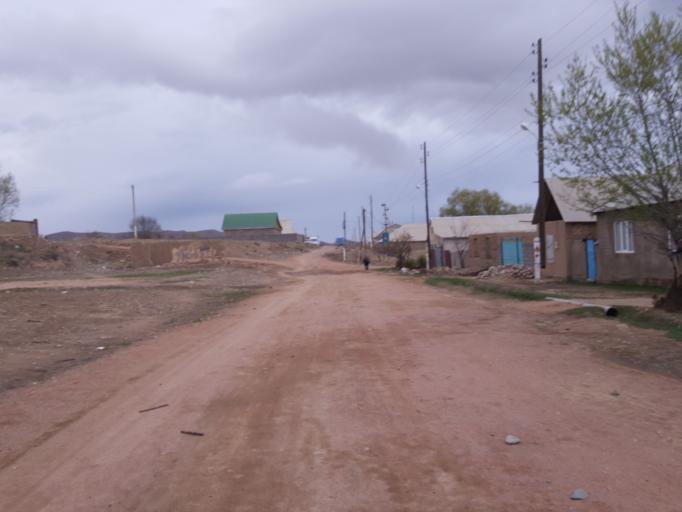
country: KG
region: Ysyk-Koel
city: Bokombayevskoye
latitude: 42.1103
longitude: 76.9810
